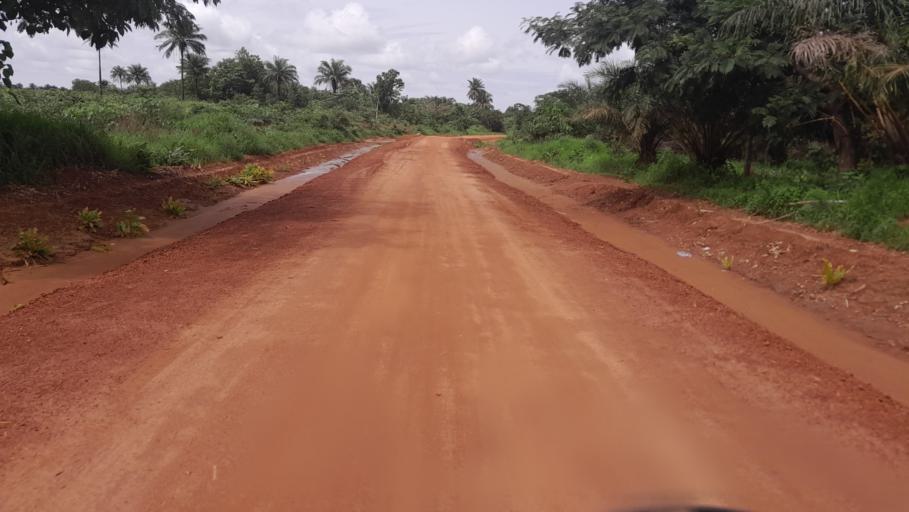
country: GN
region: Boke
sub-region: Boffa
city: Boffa
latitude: 10.0381
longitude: -13.8745
